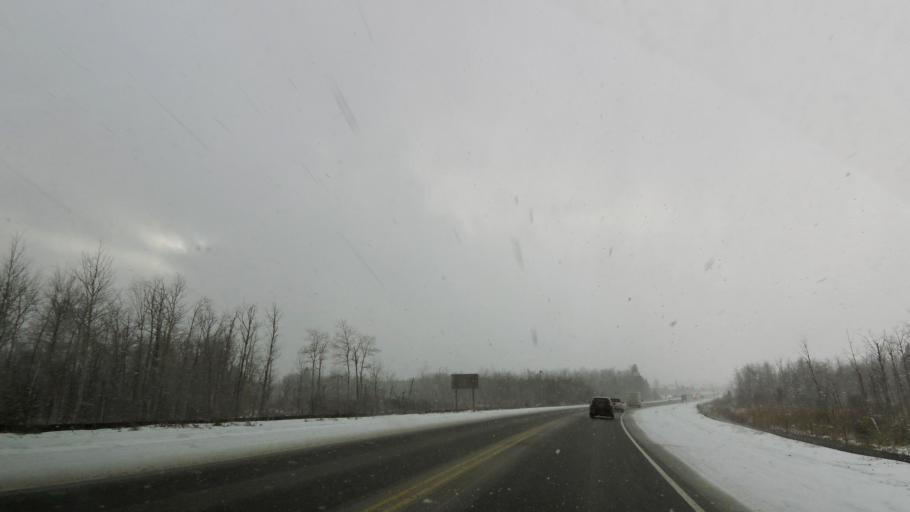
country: CA
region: Ontario
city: Orangeville
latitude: 43.8958
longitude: -80.1049
